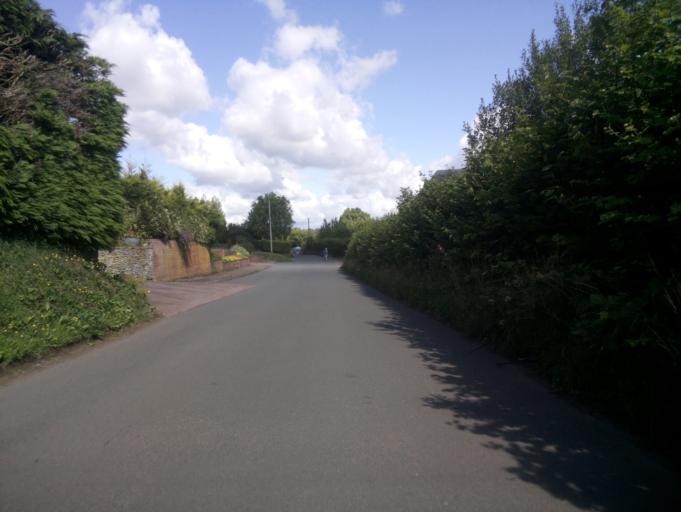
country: GB
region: England
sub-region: Gloucestershire
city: Newent
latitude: 51.9341
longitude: -2.4108
